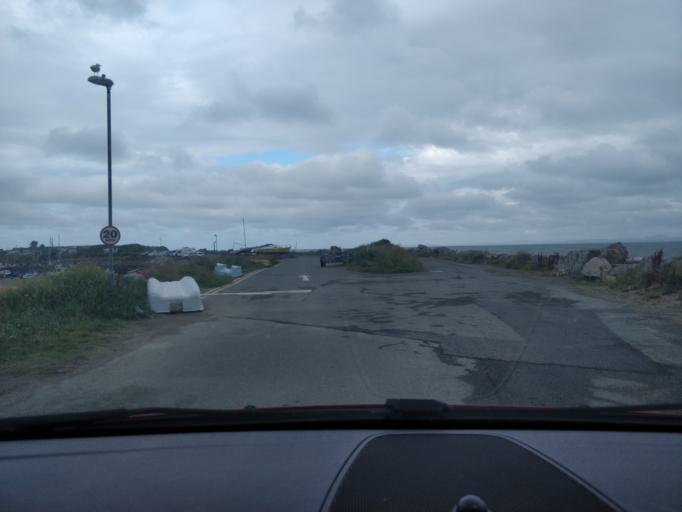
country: GB
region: Wales
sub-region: Gwynedd
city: Llanfair
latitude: 52.8261
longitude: -4.1313
